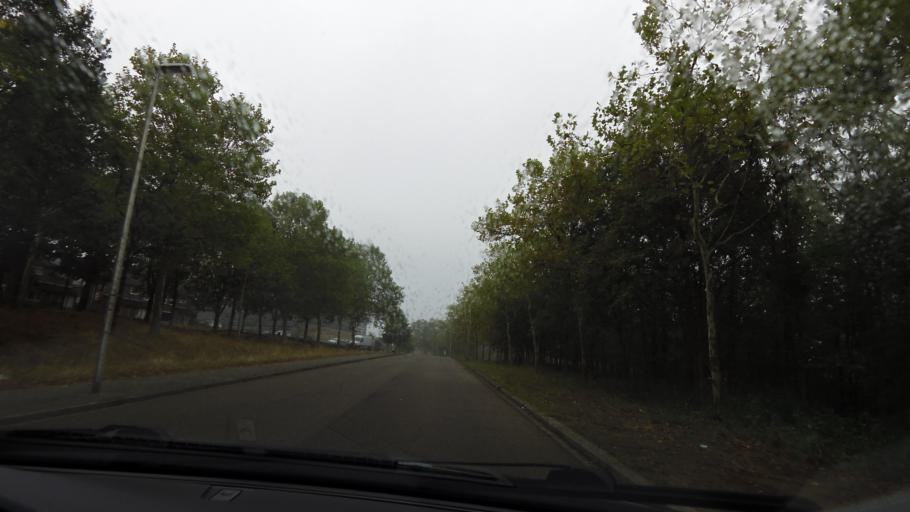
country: NL
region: Limburg
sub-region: Gemeente Heerlen
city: Heerlen
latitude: 50.8999
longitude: 5.9568
